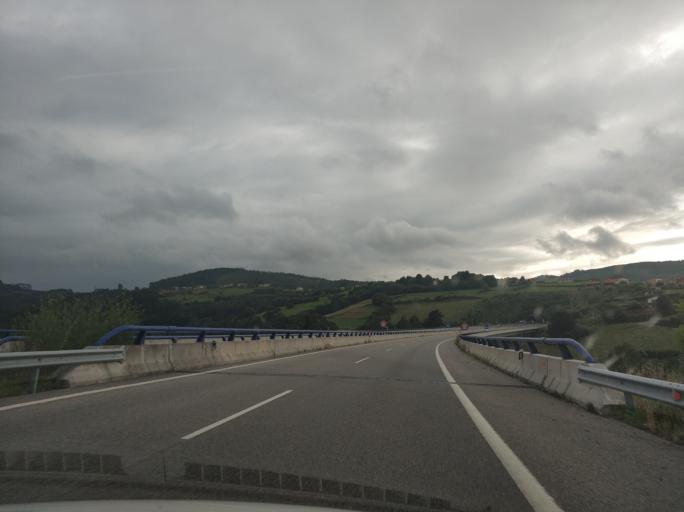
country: ES
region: Asturias
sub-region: Province of Asturias
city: Cudillero
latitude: 43.5427
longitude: -6.1456
